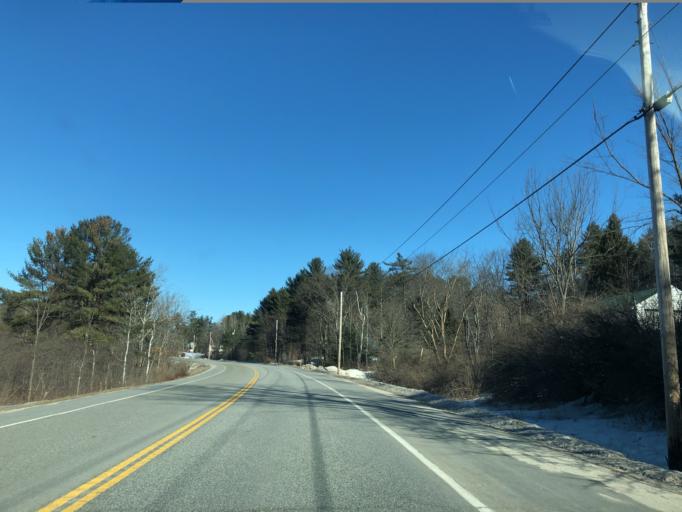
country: US
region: Maine
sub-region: Cumberland County
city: North Windham
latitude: 43.8323
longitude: -70.3821
